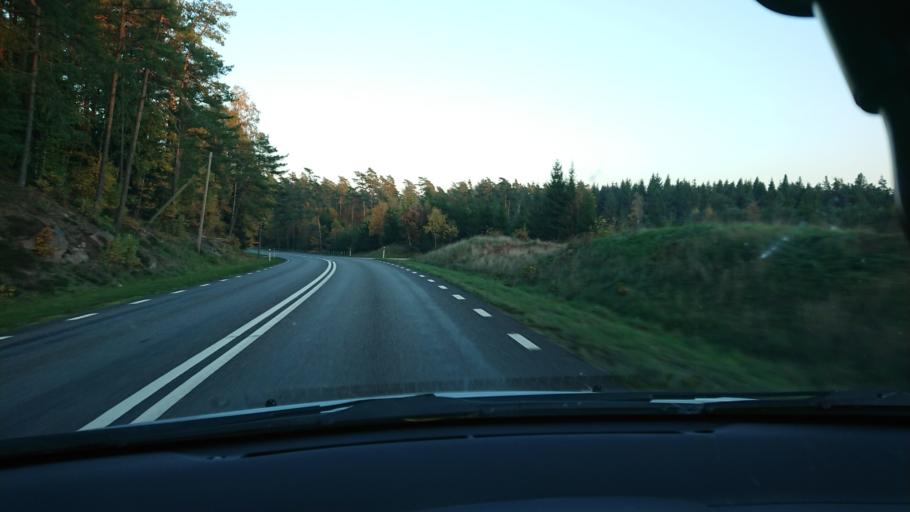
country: SE
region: Halland
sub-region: Halmstads Kommun
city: Oskarstrom
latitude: 56.7112
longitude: 13.0858
